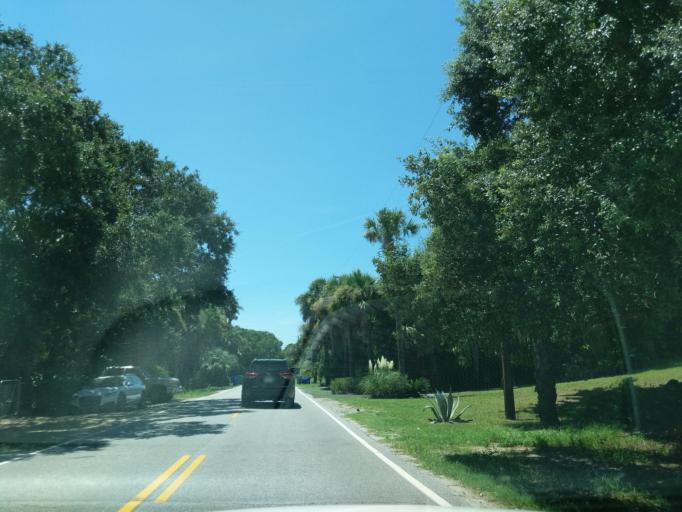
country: US
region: South Carolina
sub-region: Charleston County
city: Folly Beach
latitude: 32.6664
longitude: -79.9150
